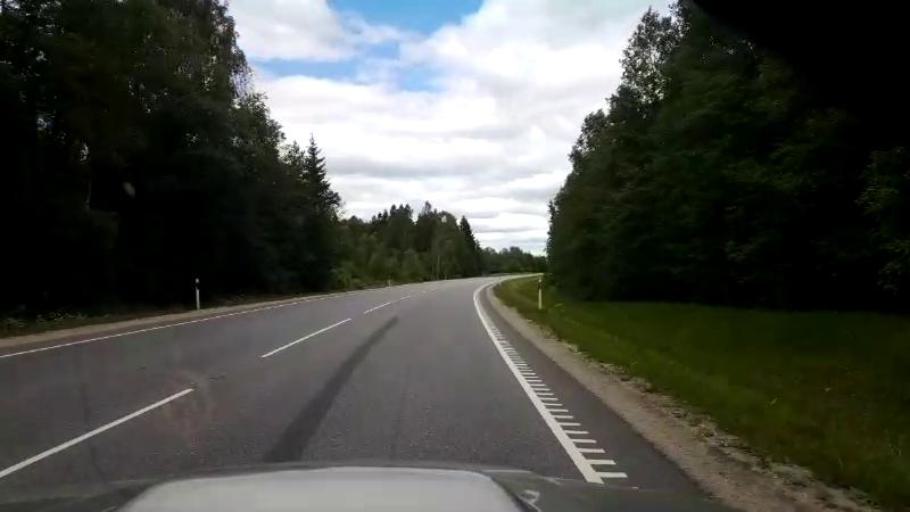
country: EE
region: Raplamaa
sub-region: Maerjamaa vald
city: Marjamaa
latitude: 58.9527
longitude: 24.4693
